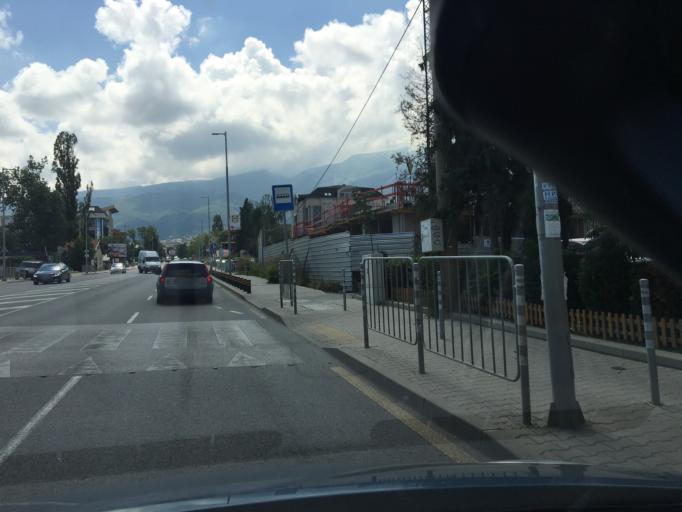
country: BG
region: Sofia-Capital
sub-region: Stolichna Obshtina
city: Sofia
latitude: 42.6484
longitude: 23.3150
